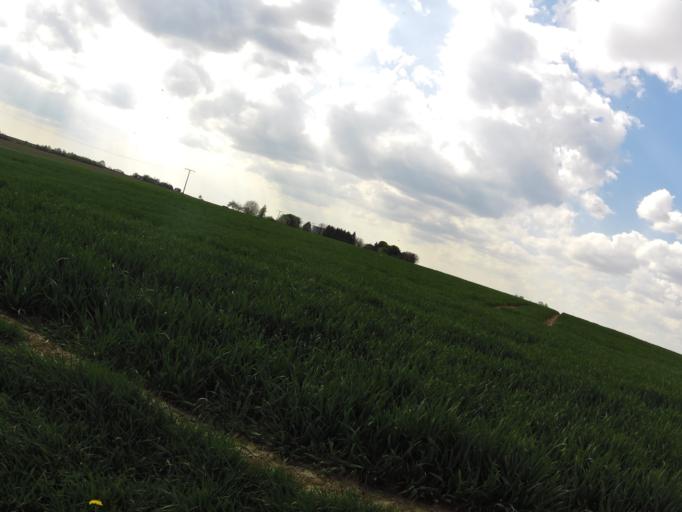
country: DE
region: Bavaria
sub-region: Regierungsbezirk Unterfranken
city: Giebelstadt
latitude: 49.6763
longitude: 9.9539
